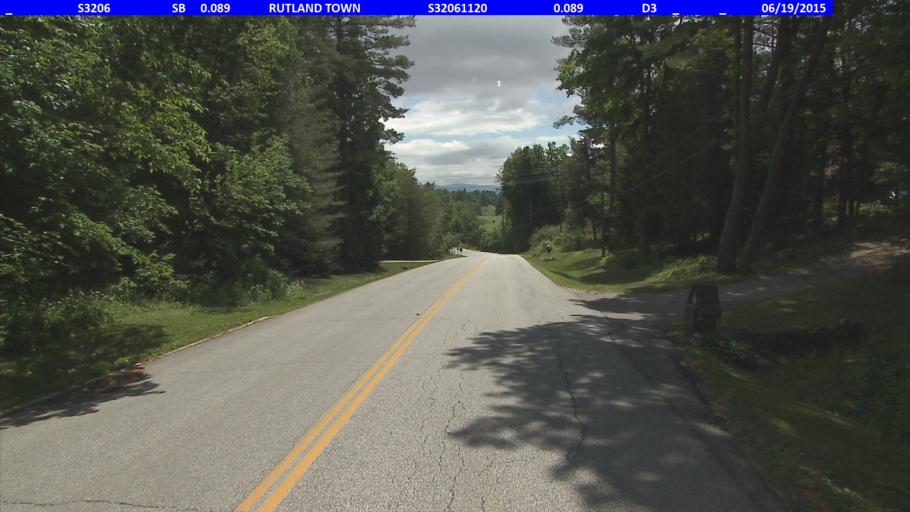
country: US
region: Vermont
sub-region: Rutland County
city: Rutland
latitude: 43.6311
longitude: -72.9887
